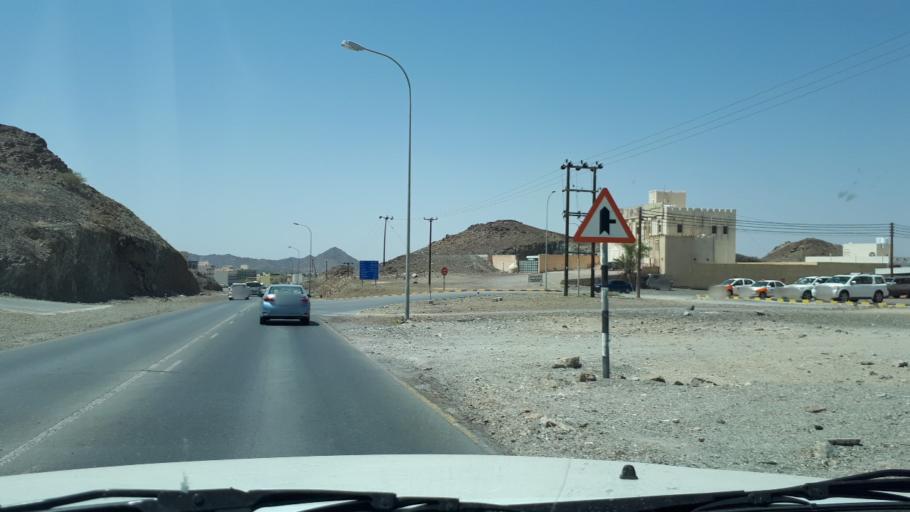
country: OM
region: Muhafazat ad Dakhiliyah
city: Bahla'
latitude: 22.9559
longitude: 57.2876
